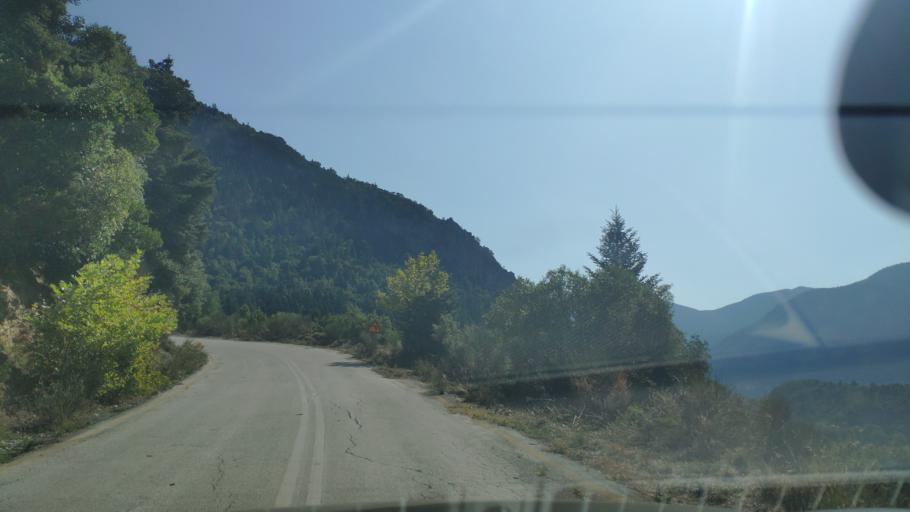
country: GR
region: Peloponnese
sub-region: Nomos Korinthias
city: Nemea
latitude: 37.8588
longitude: 22.3834
